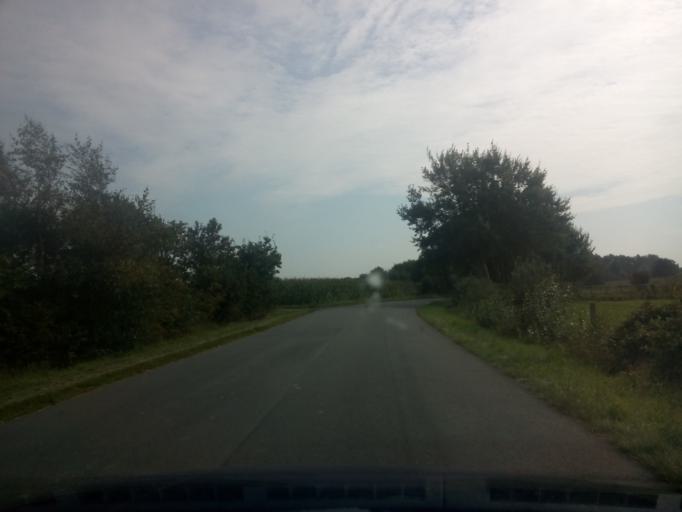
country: DE
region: Lower Saxony
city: Osterholz-Scharmbeck
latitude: 53.2479
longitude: 8.7584
